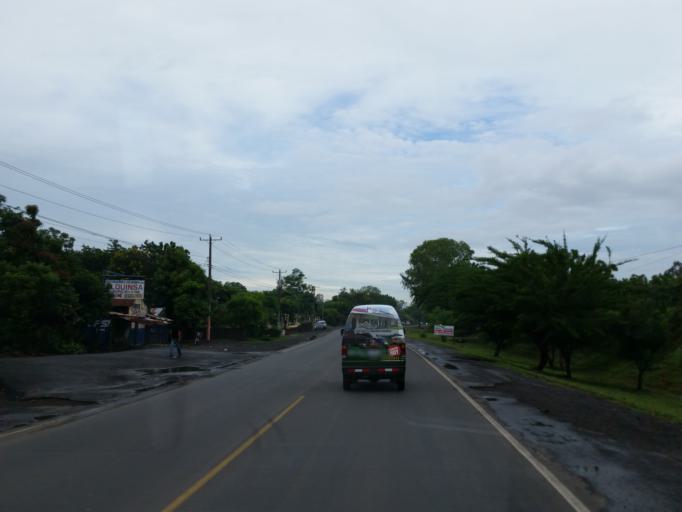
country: NI
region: Managua
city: Ciudad Sandino
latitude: 12.1970
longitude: -86.3751
